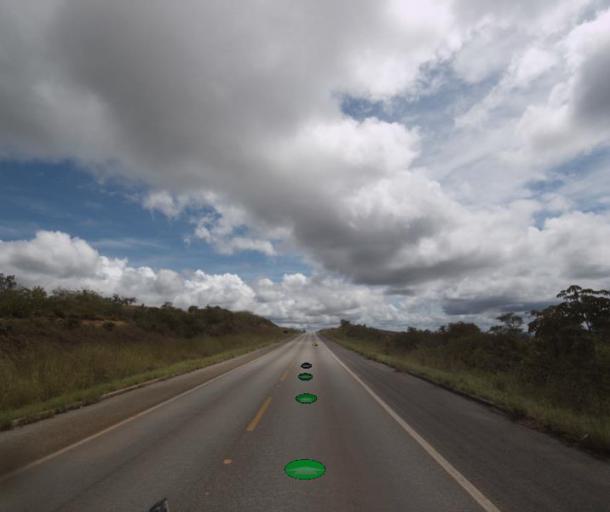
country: BR
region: Goias
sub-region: Pirenopolis
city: Pirenopolis
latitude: -15.7813
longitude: -48.4914
